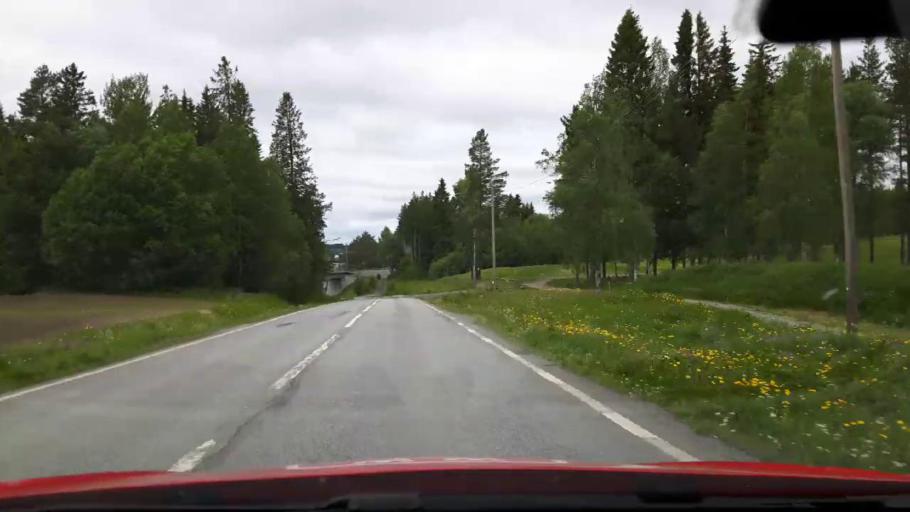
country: SE
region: Jaemtland
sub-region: Krokoms Kommun
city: Krokom
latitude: 63.2879
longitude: 14.5035
